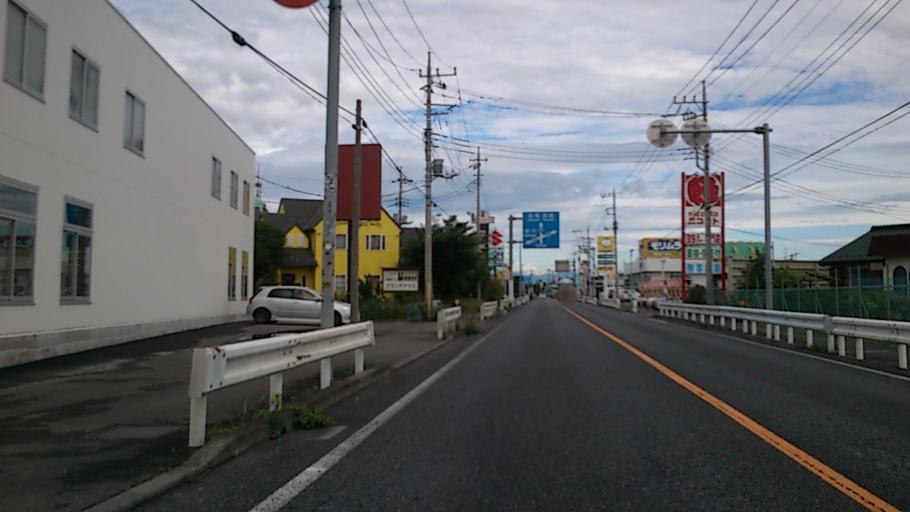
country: JP
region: Saitama
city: Honjo
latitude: 36.2587
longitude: 139.1512
